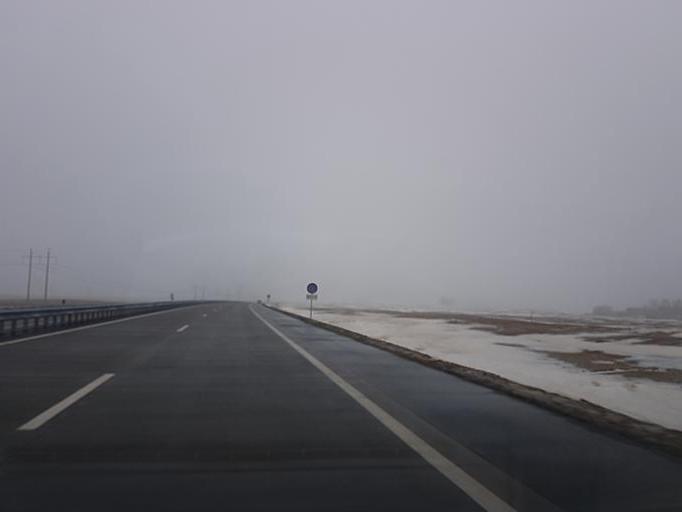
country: BY
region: Minsk
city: Atolina
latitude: 53.7333
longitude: 27.4206
